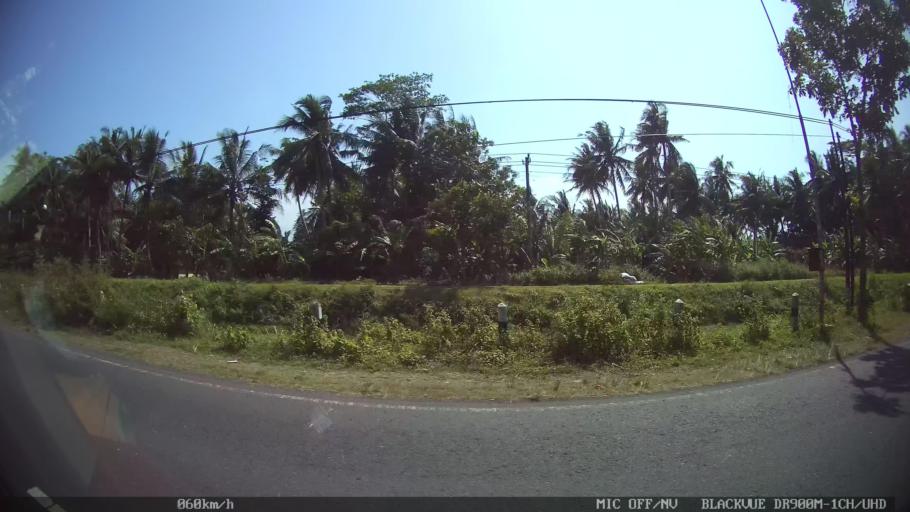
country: ID
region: Daerah Istimewa Yogyakarta
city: Srandakan
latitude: -7.9378
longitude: 110.1568
